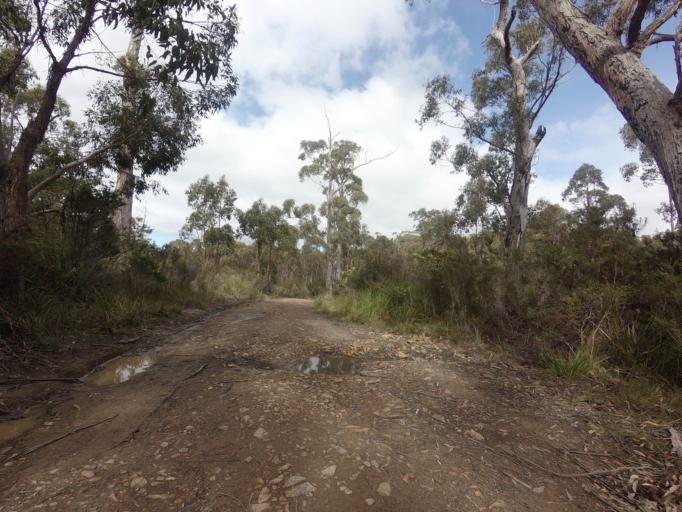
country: AU
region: Tasmania
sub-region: Huon Valley
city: Geeveston
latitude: -43.4810
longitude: 146.9383
